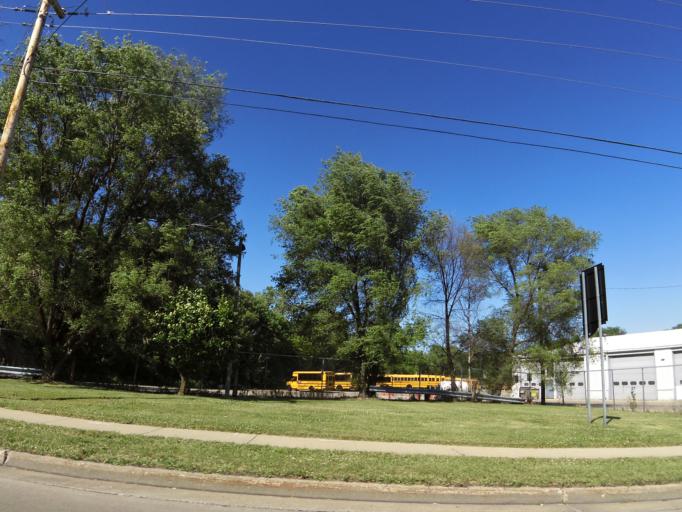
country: US
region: Wisconsin
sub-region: Rock County
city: Beloit
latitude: 42.4977
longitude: -89.0202
